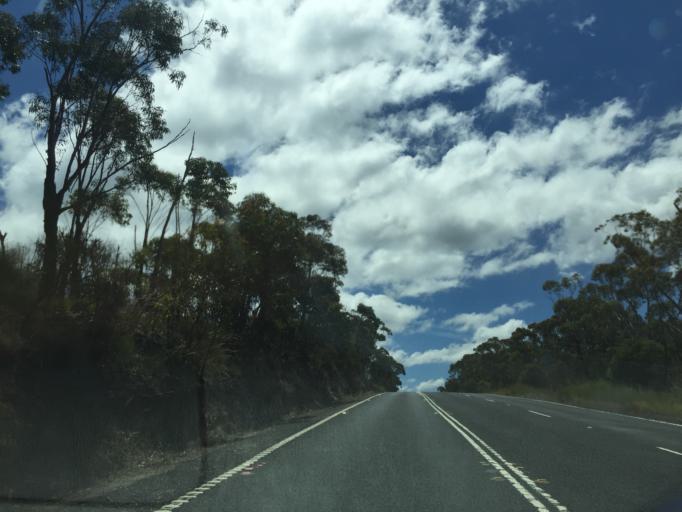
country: AU
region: New South Wales
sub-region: Blue Mountains Municipality
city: Blackheath
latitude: -33.5649
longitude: 150.3446
